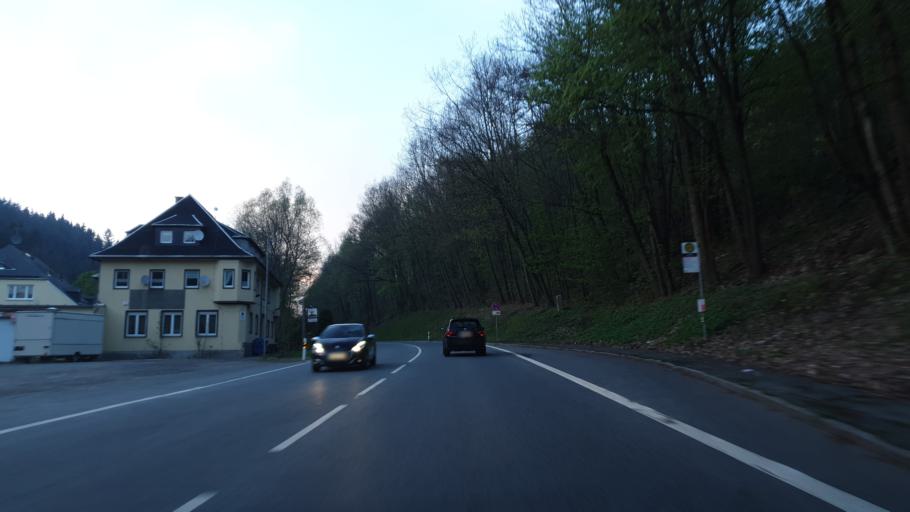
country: DE
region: Saxony
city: Aue
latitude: 50.6025
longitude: 12.7179
